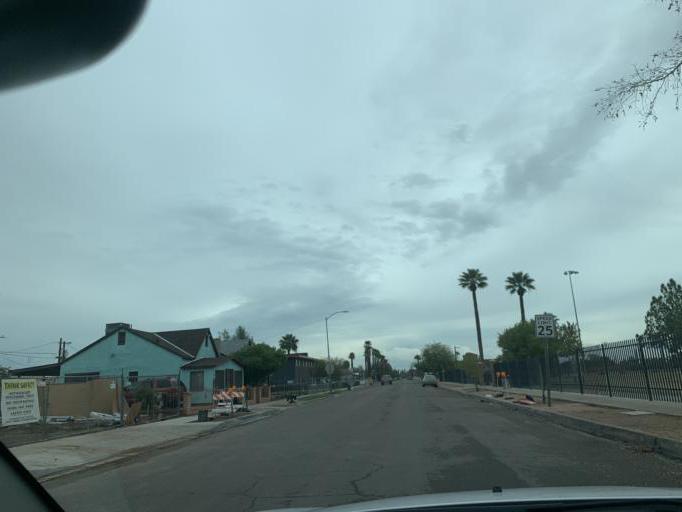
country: US
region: Arizona
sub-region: Maricopa County
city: Phoenix
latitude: 33.4529
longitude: -112.0619
